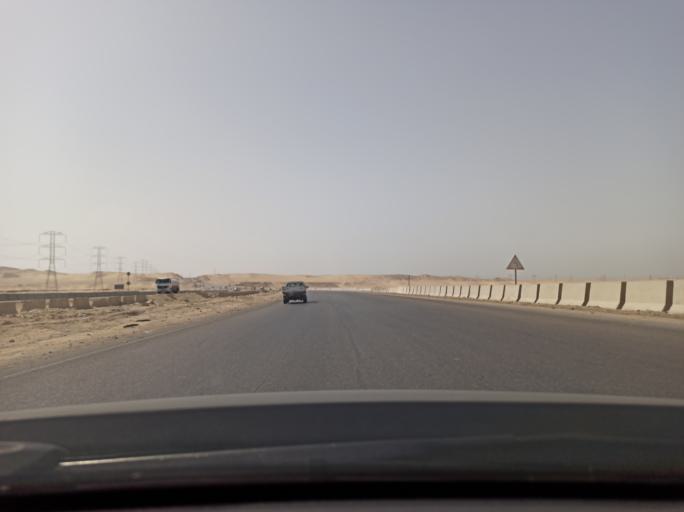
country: EG
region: Al Jizah
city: As Saff
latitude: 29.5237
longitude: 31.3835
